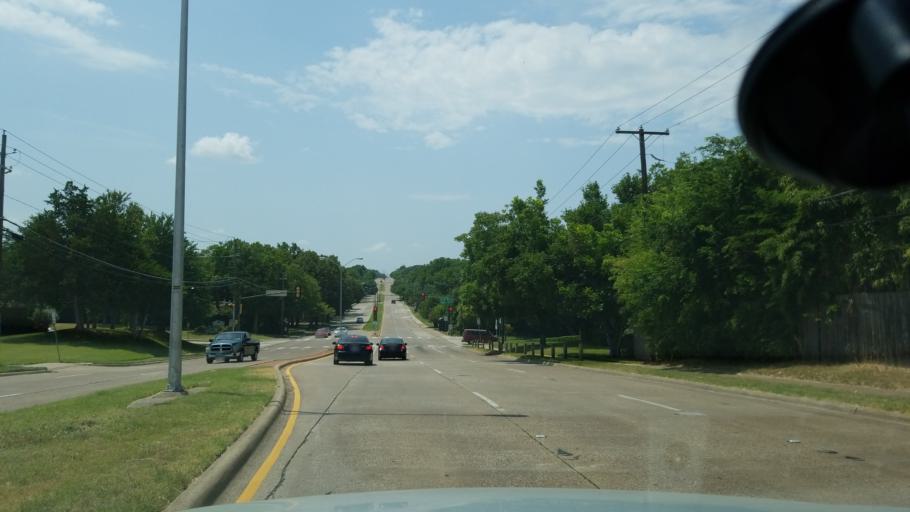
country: US
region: Texas
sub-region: Dallas County
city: Duncanville
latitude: 32.6737
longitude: -96.8401
